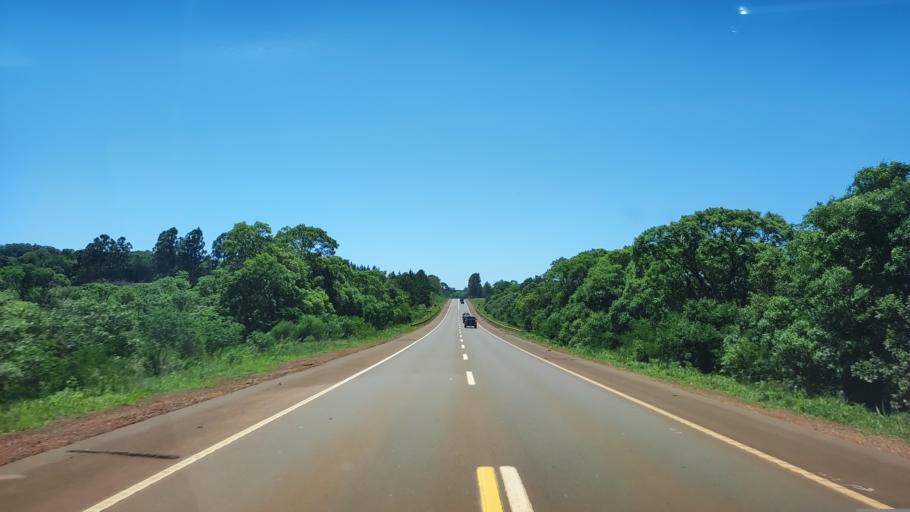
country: AR
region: Misiones
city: Aristobulo del Valle
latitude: -27.0857
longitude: -54.7981
